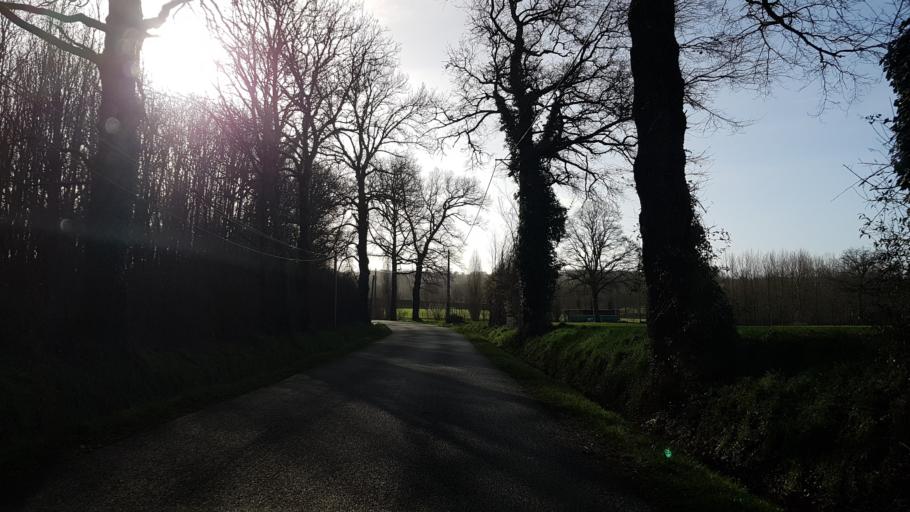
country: FR
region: Poitou-Charentes
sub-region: Departement de la Charente
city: Etagnac
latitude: 45.9464
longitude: 0.7859
